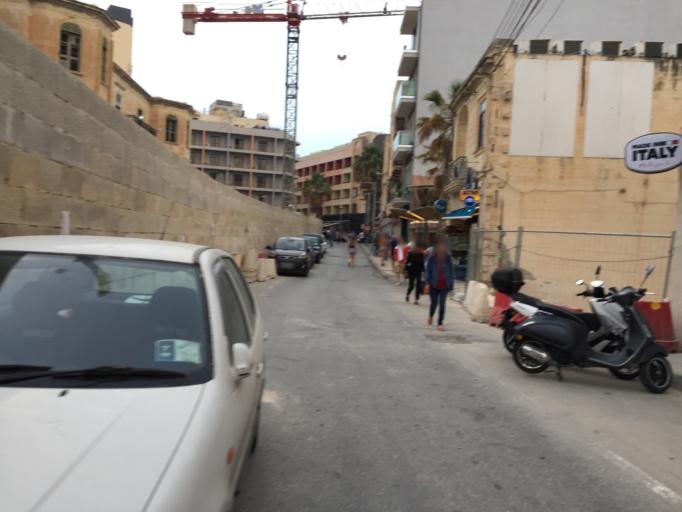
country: MT
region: Saint Julian
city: San Giljan
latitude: 35.9228
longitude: 14.4898
